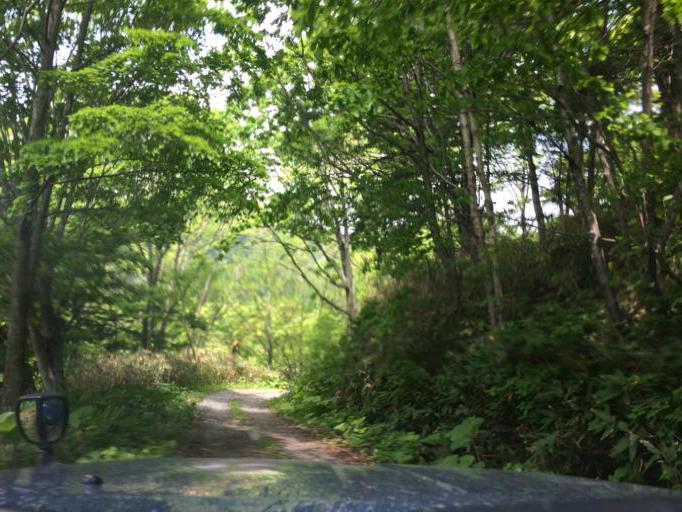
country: JP
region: Hokkaido
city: Niseko Town
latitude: 42.6451
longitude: 140.5806
